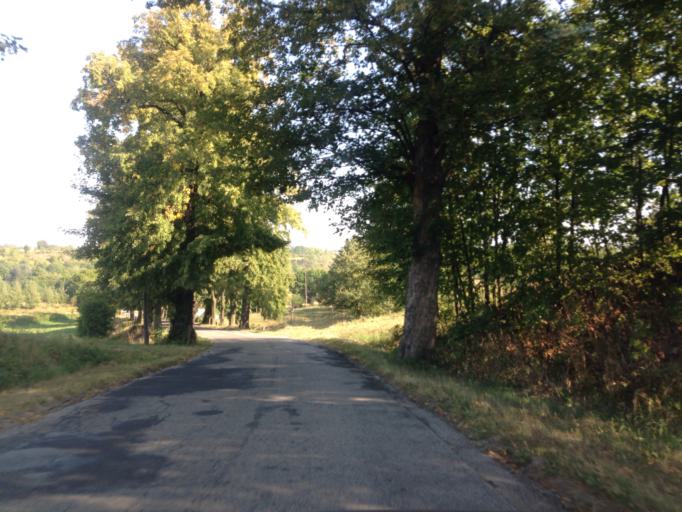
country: PL
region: Kujawsko-Pomorskie
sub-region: Powiat brodnicki
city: Brzozie
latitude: 53.3010
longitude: 19.6149
